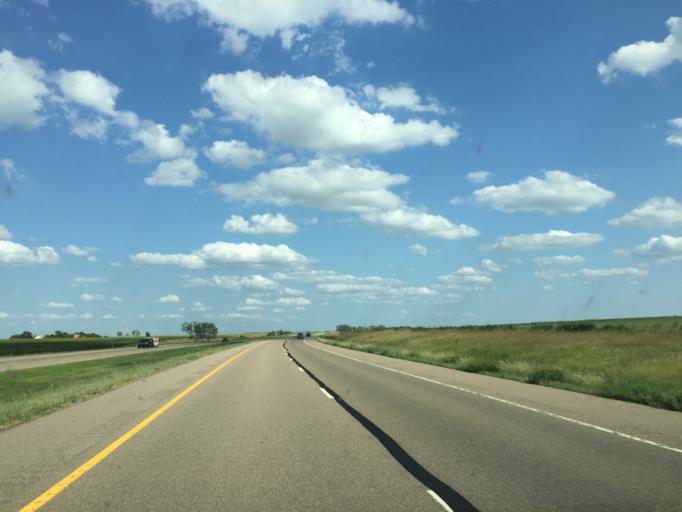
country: US
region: Kansas
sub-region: Gove County
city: Gove
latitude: 39.0960
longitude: -100.3233
